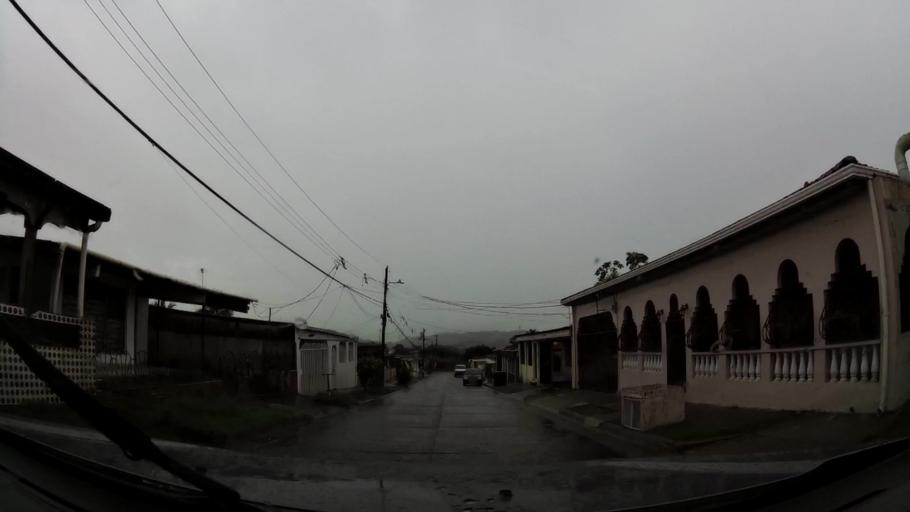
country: PA
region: Colon
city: Puerto Pilon
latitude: 9.3573
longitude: -79.7929
